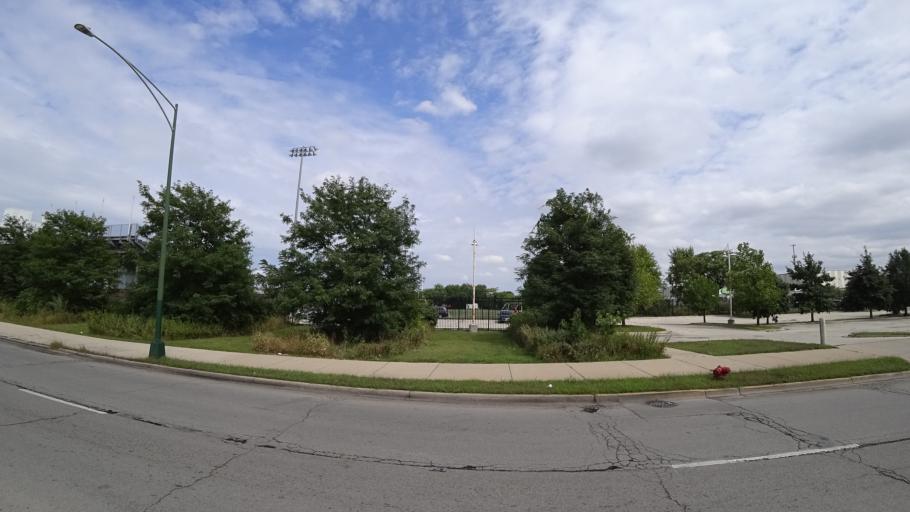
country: US
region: Illinois
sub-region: Cook County
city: Cicero
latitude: 41.8663
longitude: -87.7643
